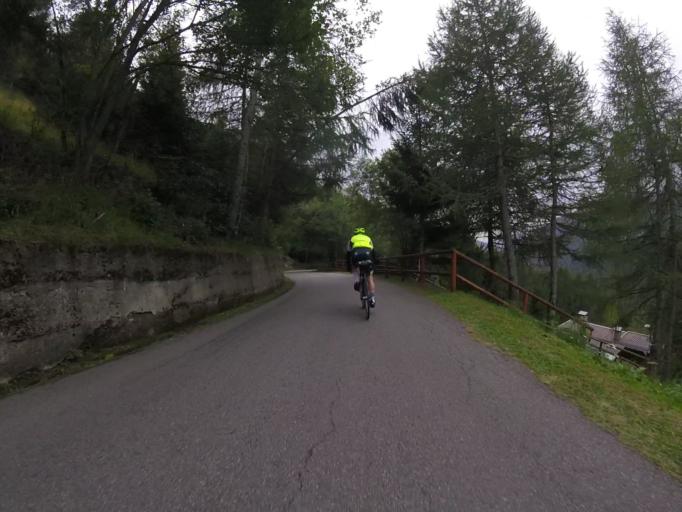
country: IT
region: Lombardy
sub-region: Provincia di Brescia
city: Monno
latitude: 46.2365
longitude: 10.3208
